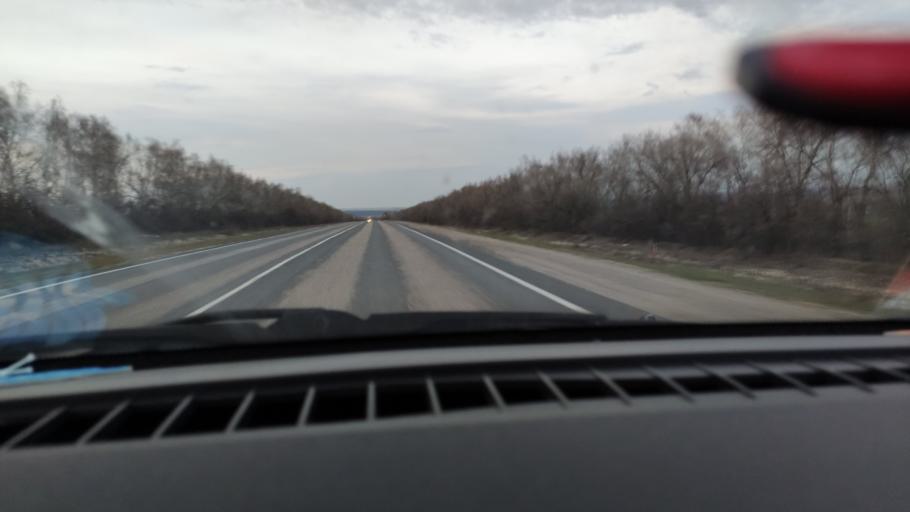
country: RU
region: Saratov
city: Sinodskoye
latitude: 51.9475
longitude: 46.6044
